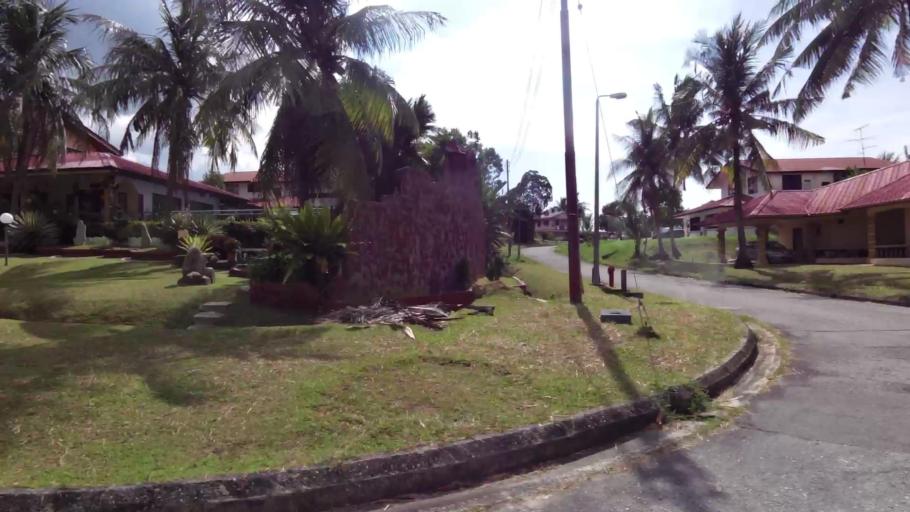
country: BN
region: Brunei and Muara
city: Bandar Seri Begawan
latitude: 4.9579
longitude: 114.9591
